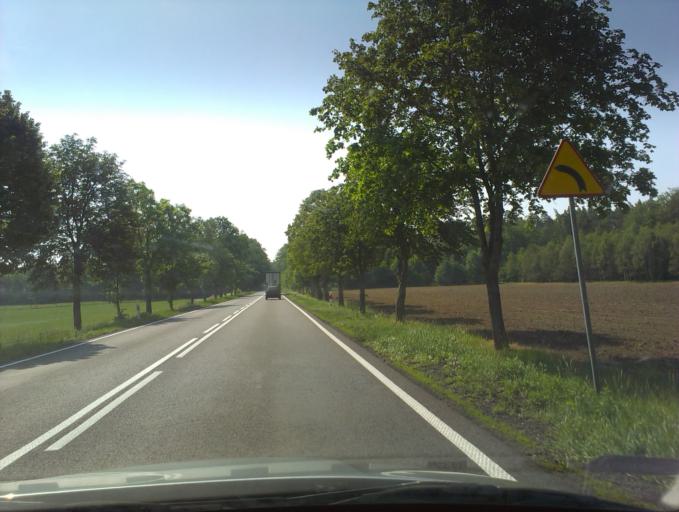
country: PL
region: West Pomeranian Voivodeship
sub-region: Powiat szczecinecki
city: Szczecinek
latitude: 53.6406
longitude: 16.7604
